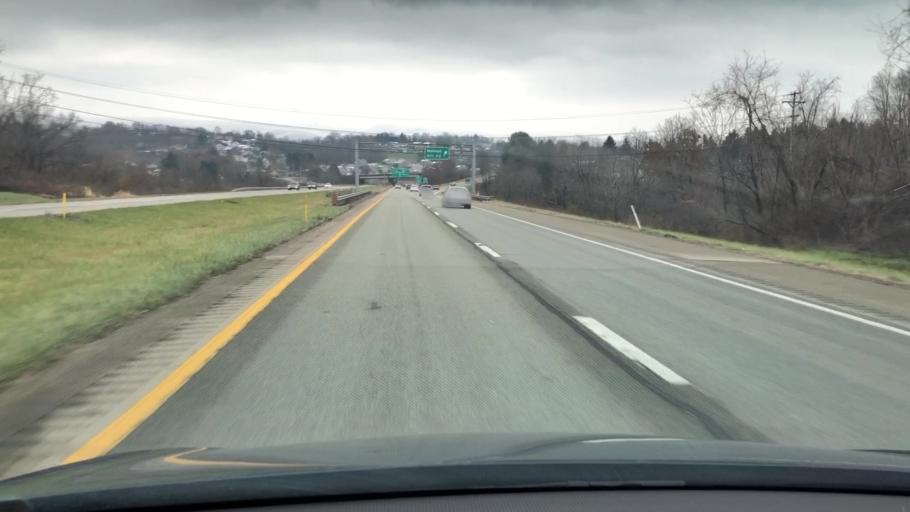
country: US
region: Pennsylvania
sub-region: Fayette County
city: South Uniontown
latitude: 39.8863
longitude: -79.7496
